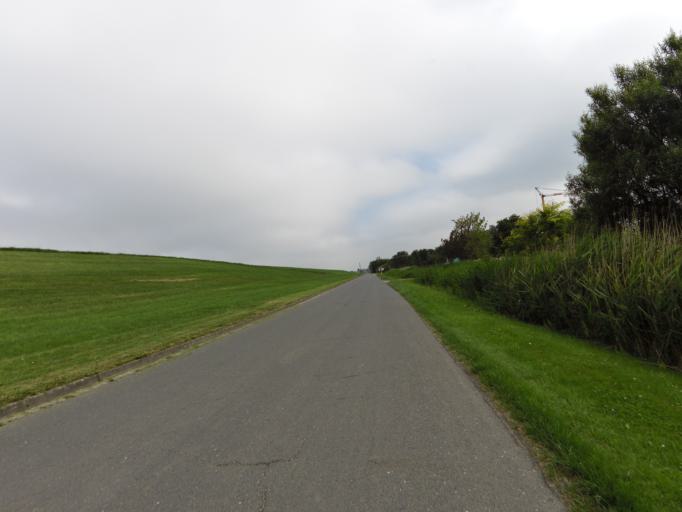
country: DE
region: Lower Saxony
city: Padingbuttel
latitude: 53.7440
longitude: 8.5265
